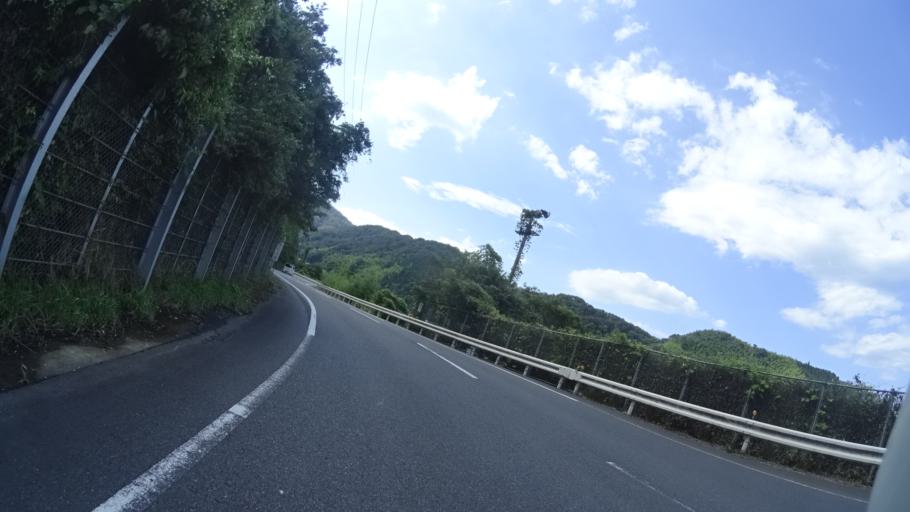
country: JP
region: Kyoto
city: Maizuru
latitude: 35.4705
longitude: 135.3187
